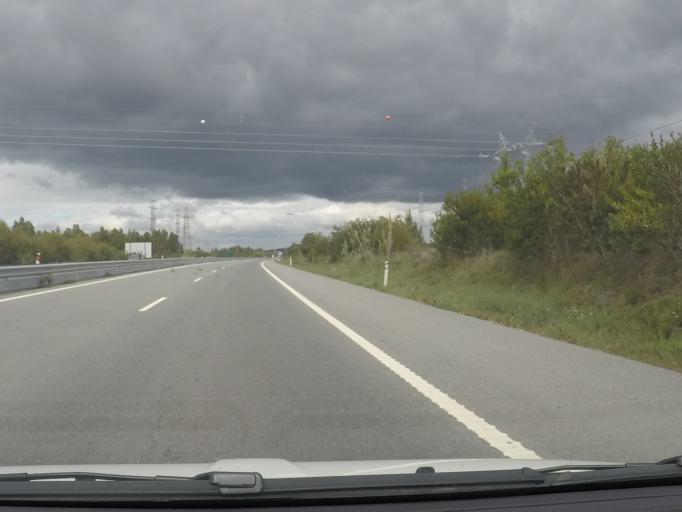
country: PT
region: Setubal
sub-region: Santiago do Cacem
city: Santo Andre
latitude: 37.9925
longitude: -8.7664
